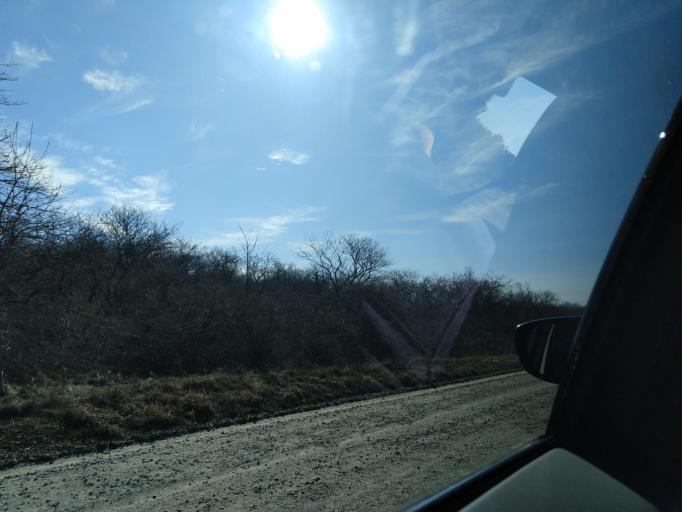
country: US
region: Massachusetts
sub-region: Essex County
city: Ipswich
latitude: 42.7396
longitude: -70.7929
